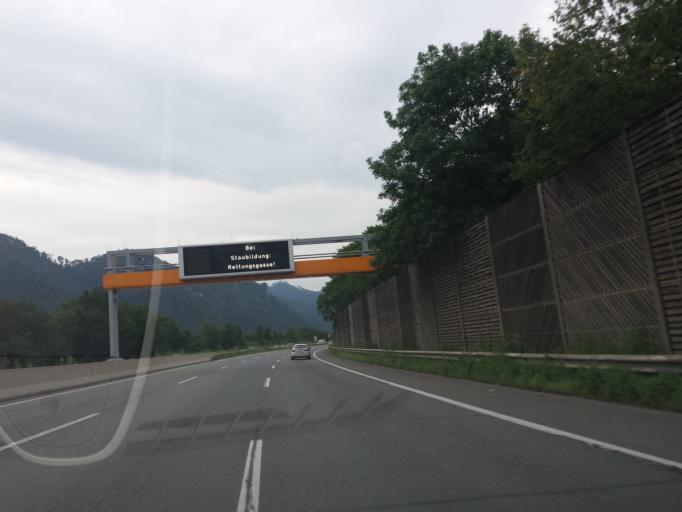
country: AT
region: Styria
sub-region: Politischer Bezirk Graz-Umgebung
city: Deutschfeistritz
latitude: 47.1540
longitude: 15.3260
